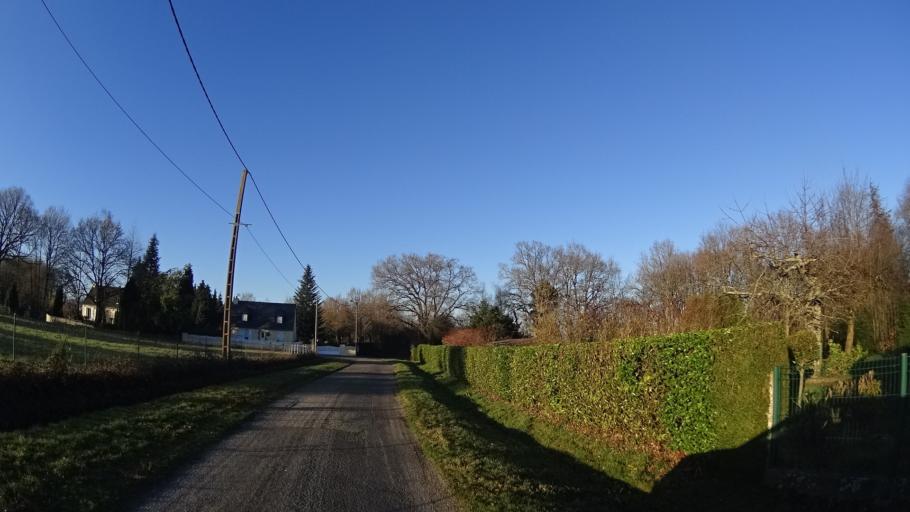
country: FR
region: Brittany
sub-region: Departement du Morbihan
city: Saint-Jean-la-Poterie
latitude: 47.6355
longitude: -2.1140
